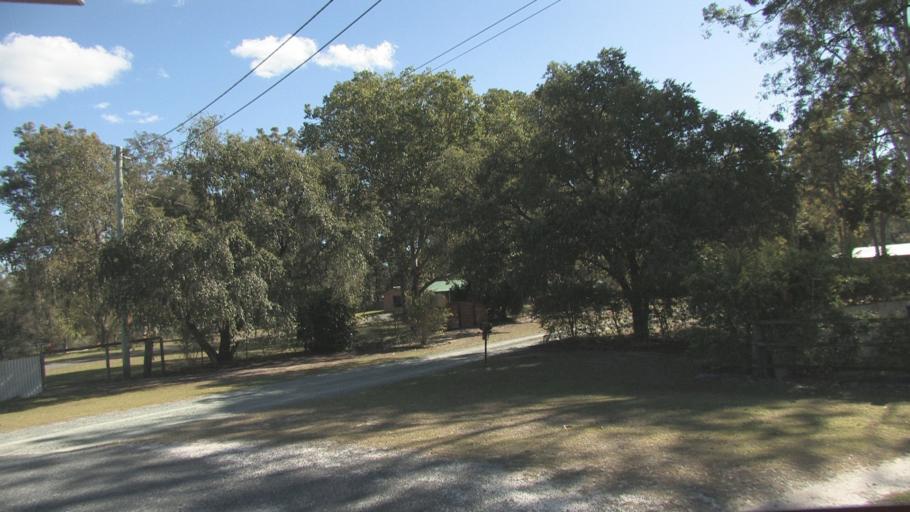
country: AU
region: Queensland
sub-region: Logan
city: Chambers Flat
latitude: -27.7456
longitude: 153.0977
